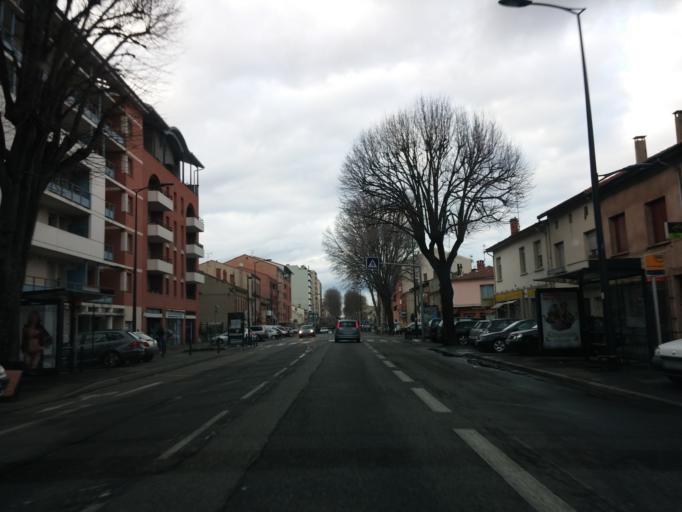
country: FR
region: Midi-Pyrenees
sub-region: Departement de la Haute-Garonne
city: Toulouse
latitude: 43.5774
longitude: 1.4506
